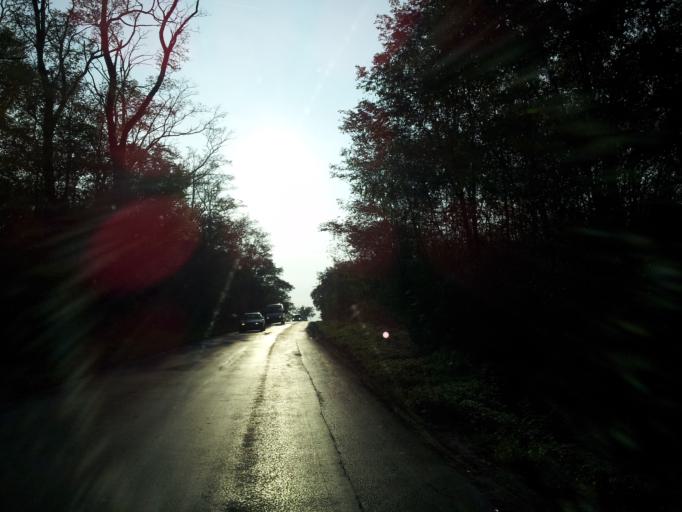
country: HU
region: Komarom-Esztergom
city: Kisber
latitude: 47.4850
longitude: 18.0727
